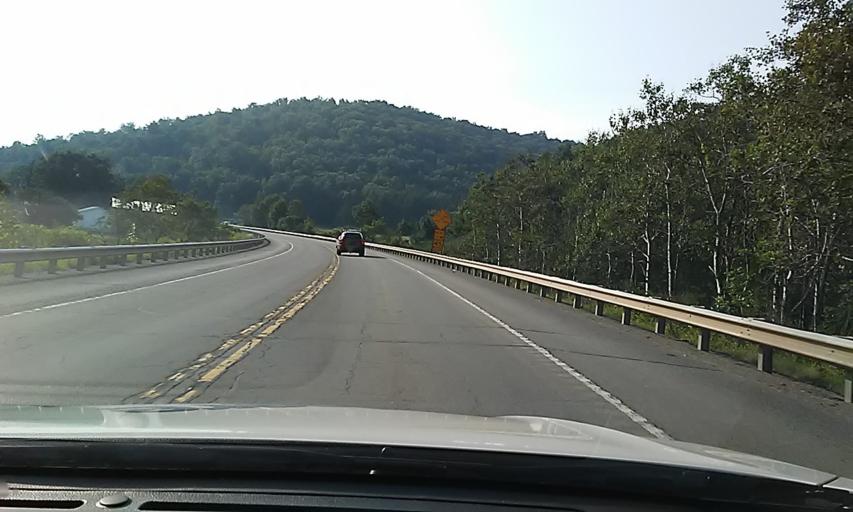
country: US
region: Pennsylvania
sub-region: Potter County
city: Coudersport
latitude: 41.7762
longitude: -78.1320
